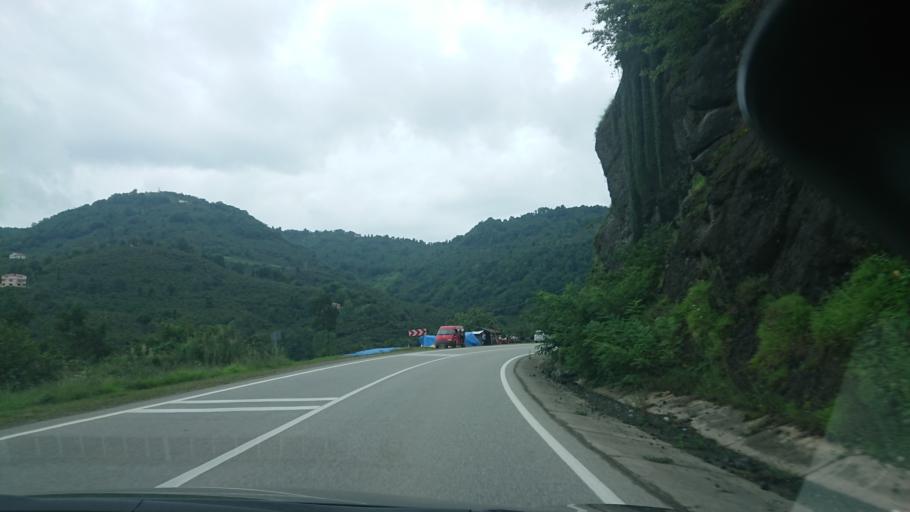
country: TR
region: Giresun
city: Guce
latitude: 40.9387
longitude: 38.8593
